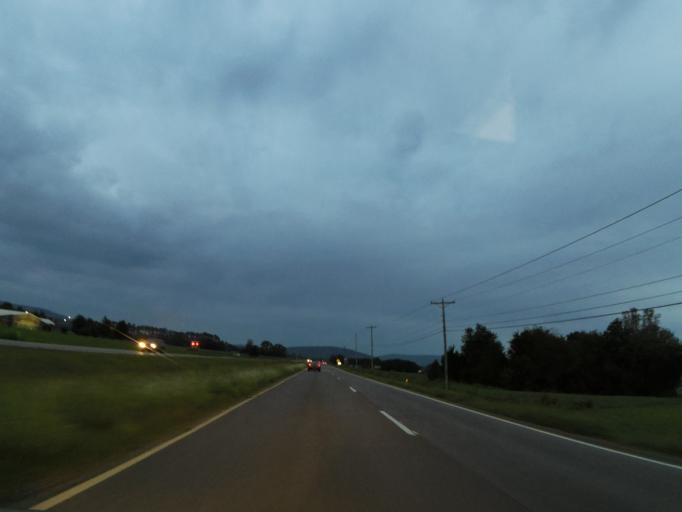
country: US
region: Alabama
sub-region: Madison County
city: Moores Mill
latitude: 34.7374
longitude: -86.4350
